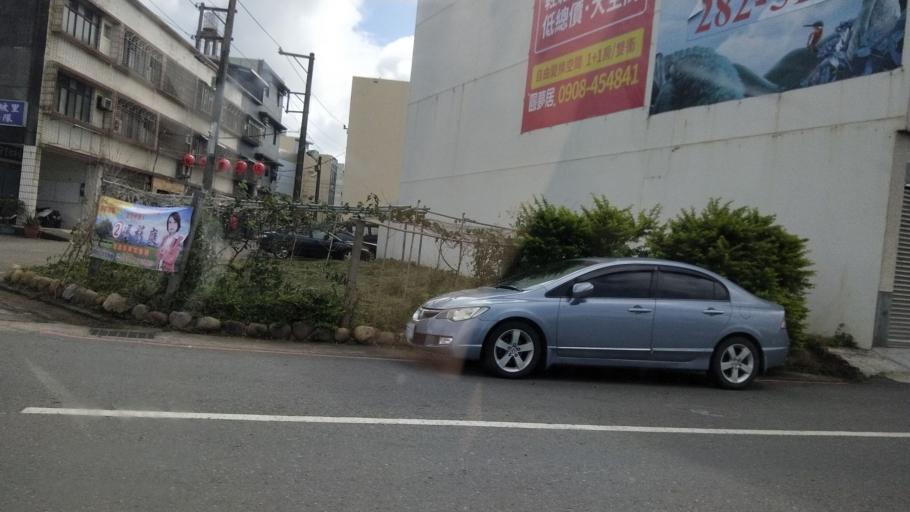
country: TW
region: Taiwan
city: Taoyuan City
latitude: 25.0160
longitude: 121.1350
